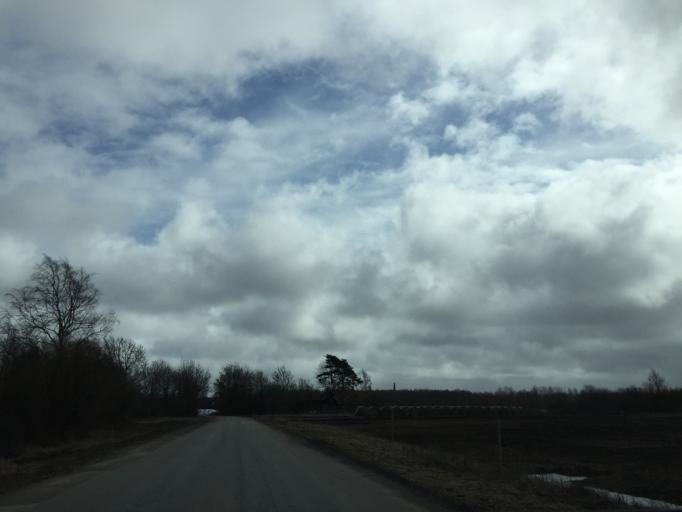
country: EE
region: Laeaene
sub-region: Lihula vald
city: Lihula
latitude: 58.7341
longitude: 23.8612
